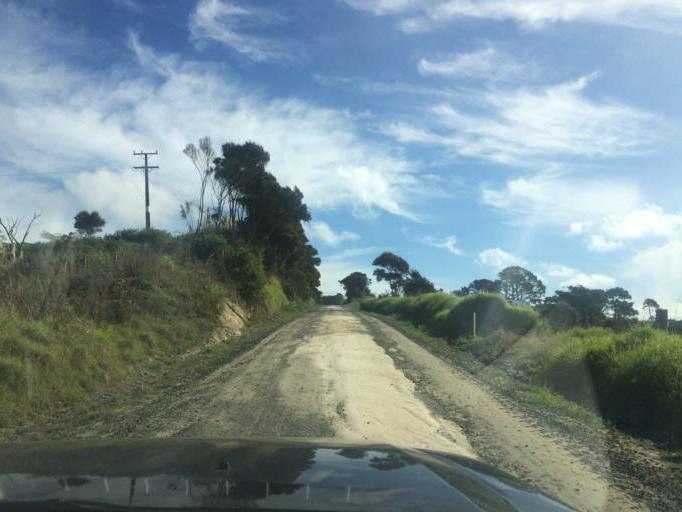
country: NZ
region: Northland
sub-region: Kaipara District
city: Dargaville
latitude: -36.0278
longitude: 173.8701
